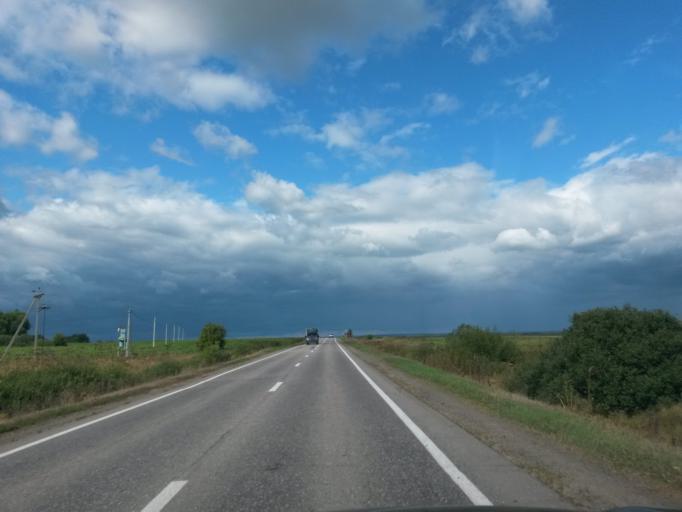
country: RU
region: Jaroslavl
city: Yaroslavl
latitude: 57.7564
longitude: 39.8709
